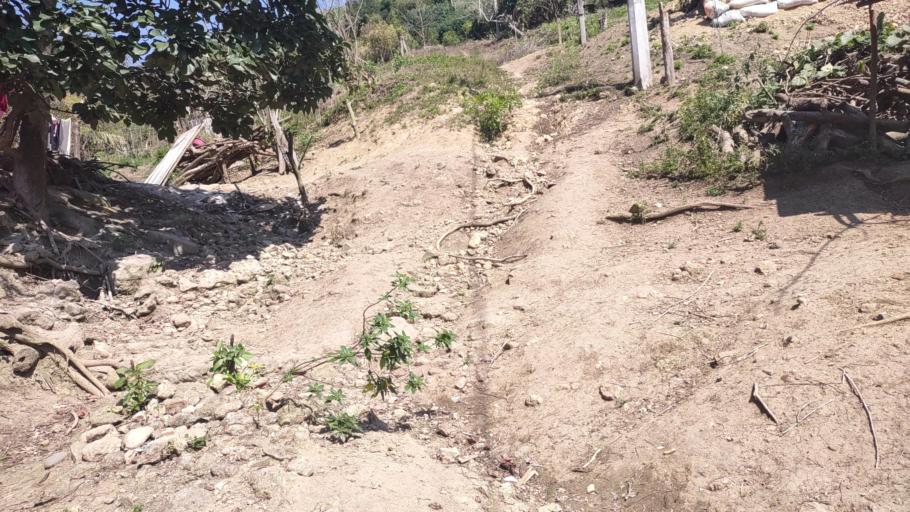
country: MX
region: Veracruz
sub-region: Papantla
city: Polutla
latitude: 20.5031
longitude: -97.2173
